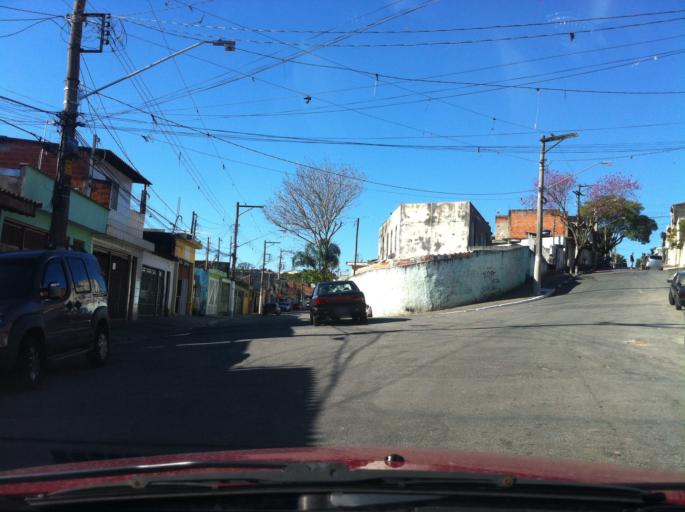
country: BR
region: Sao Paulo
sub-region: Ferraz De Vasconcelos
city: Ferraz de Vasconcelos
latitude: -23.5595
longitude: -46.4076
